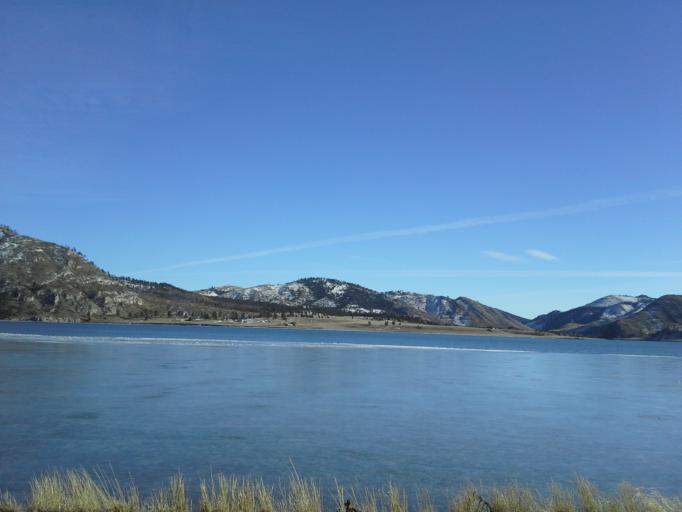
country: US
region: Montana
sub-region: Lewis and Clark County
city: Helena Valley Northeast
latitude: 46.8309
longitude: -111.9548
